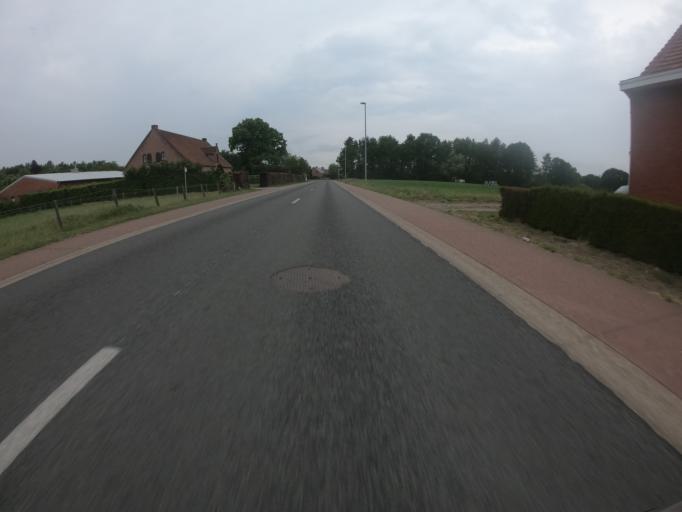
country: BE
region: Flanders
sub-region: Provincie Antwerpen
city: Laakdal
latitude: 51.0660
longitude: 5.0136
